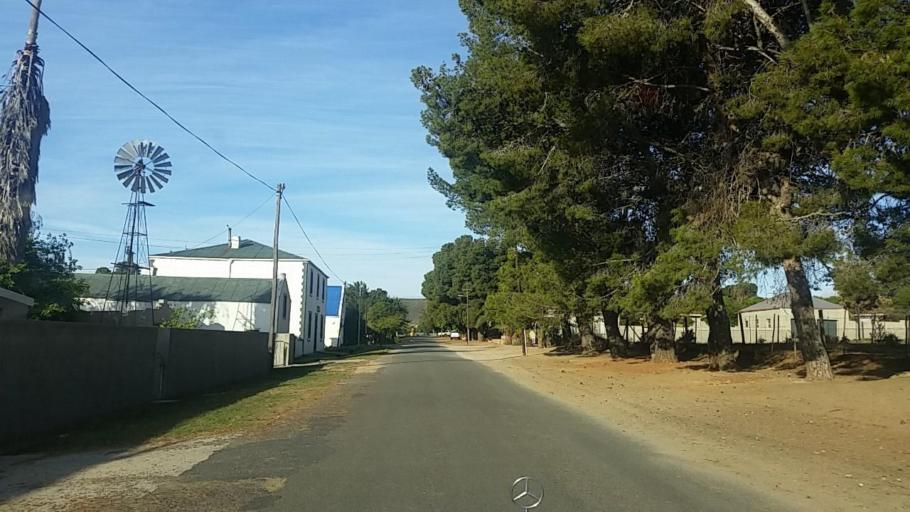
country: ZA
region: Western Cape
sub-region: Eden District Municipality
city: Knysna
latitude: -33.6547
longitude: 23.1272
